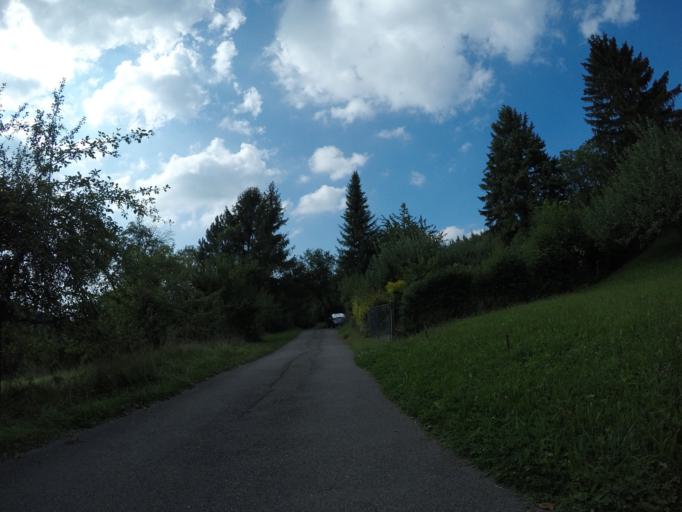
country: DE
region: Baden-Wuerttemberg
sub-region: Tuebingen Region
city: Reutlingen
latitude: 48.4636
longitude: 9.1982
